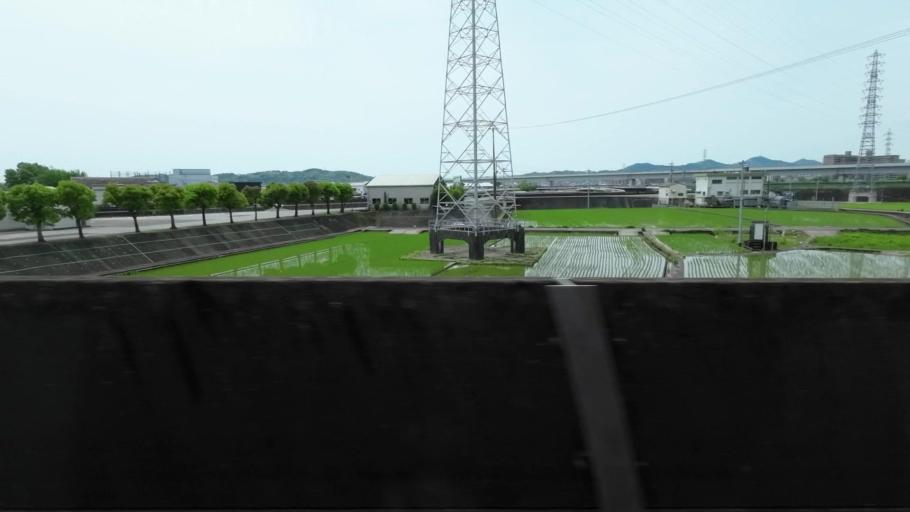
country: JP
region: Kochi
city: Kochi-shi
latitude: 33.5810
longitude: 133.5713
